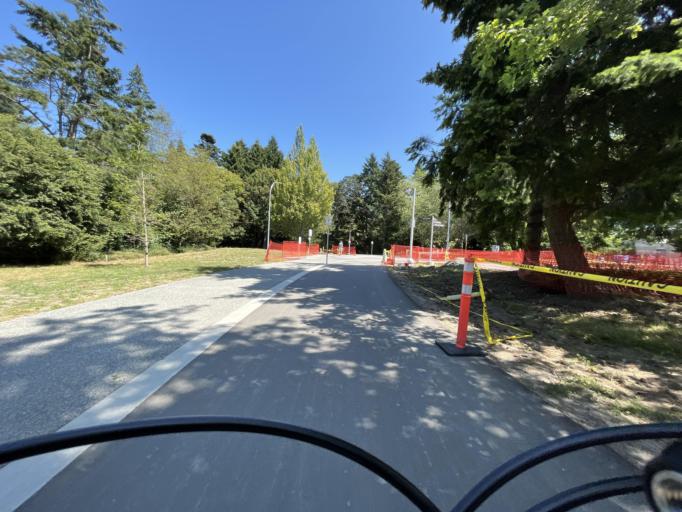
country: CA
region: British Columbia
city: Oak Bay
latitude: 48.4633
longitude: -123.3188
